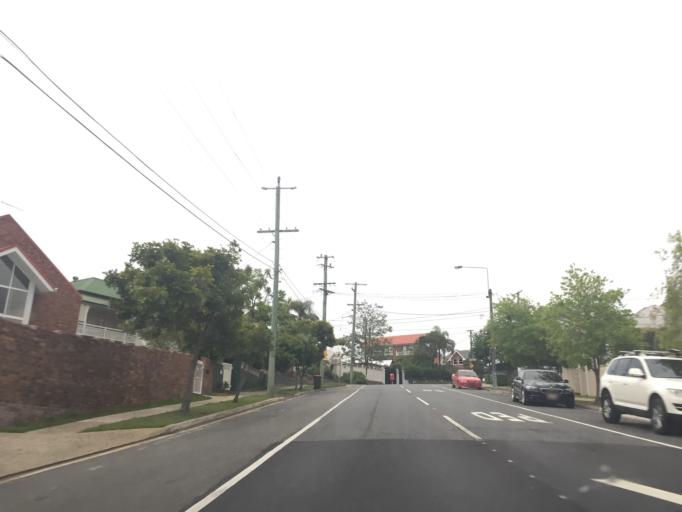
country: AU
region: Queensland
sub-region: Brisbane
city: Milton
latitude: -27.4596
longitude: 152.9919
